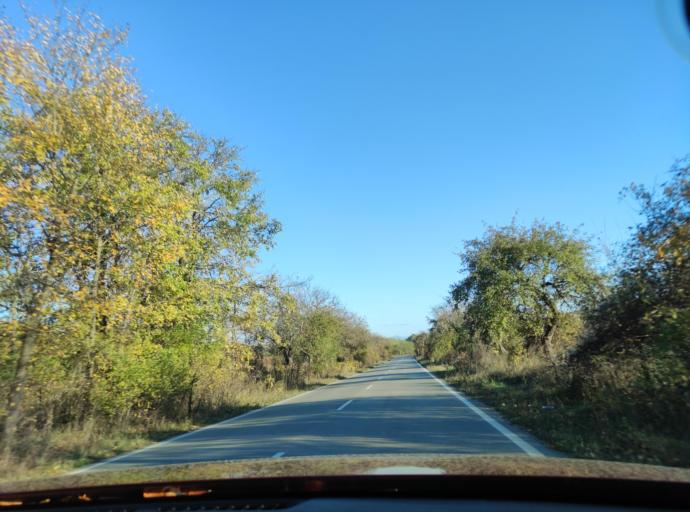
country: BG
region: Montana
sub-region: Obshtina Chiprovtsi
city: Chiprovtsi
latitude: 43.4212
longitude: 23.0185
